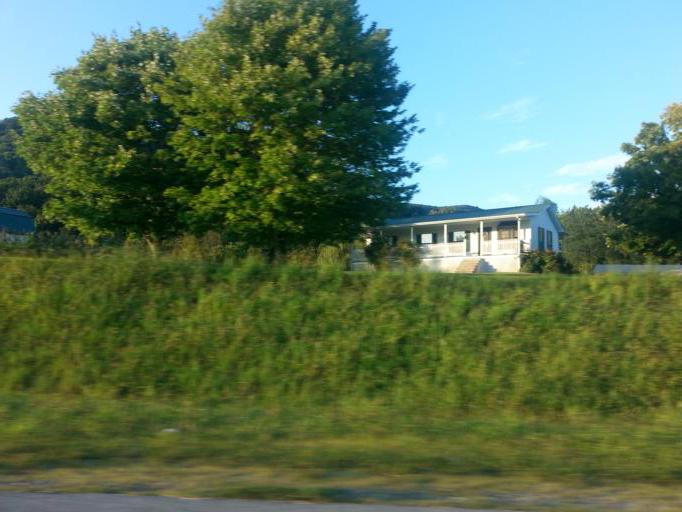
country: US
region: Tennessee
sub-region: Grainger County
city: Blaine
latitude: 36.1588
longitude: -83.7275
